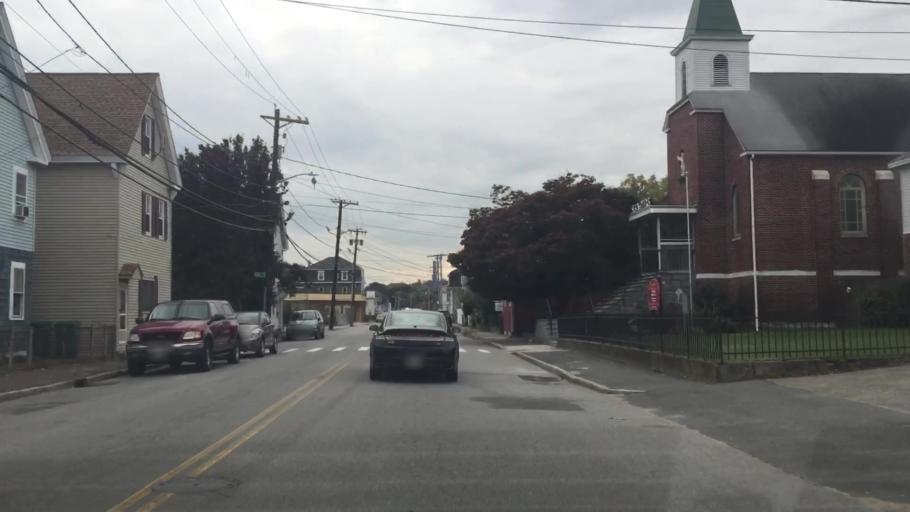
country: US
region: Massachusetts
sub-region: Middlesex County
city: Lowell
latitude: 42.6516
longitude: -71.3085
